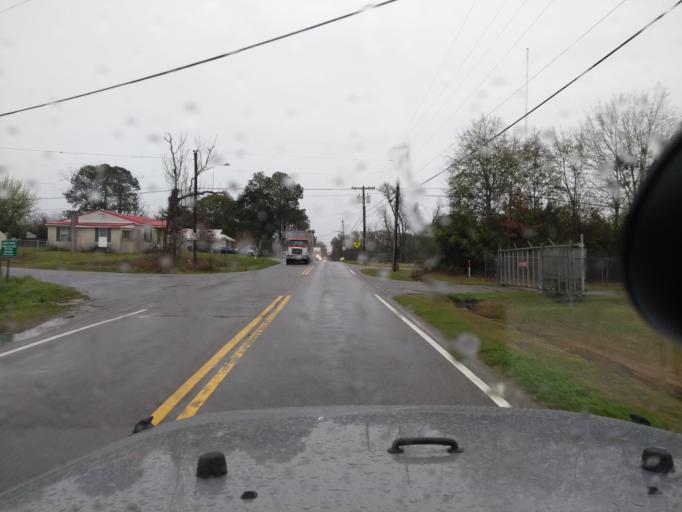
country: US
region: Georgia
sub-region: Chatham County
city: Garden City
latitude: 32.0914
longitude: -81.1474
